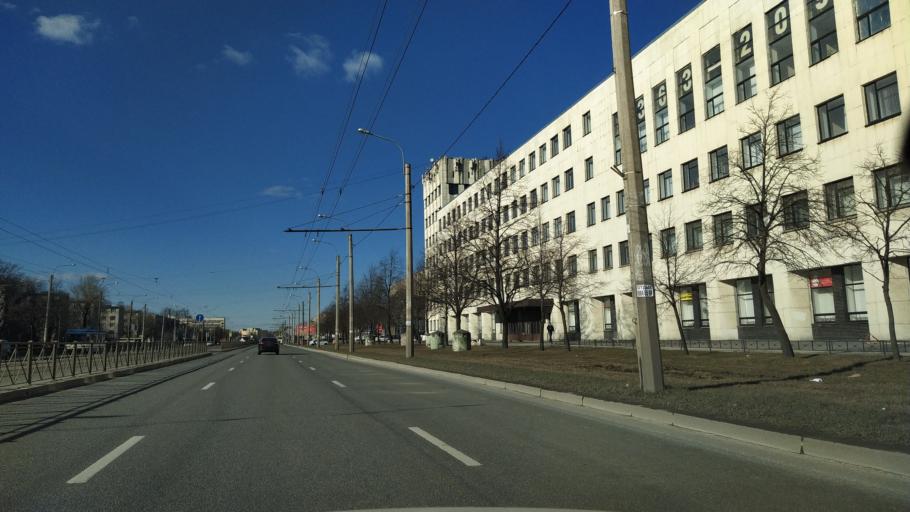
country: RU
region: St.-Petersburg
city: Kupchino
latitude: 59.8856
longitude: 30.3656
